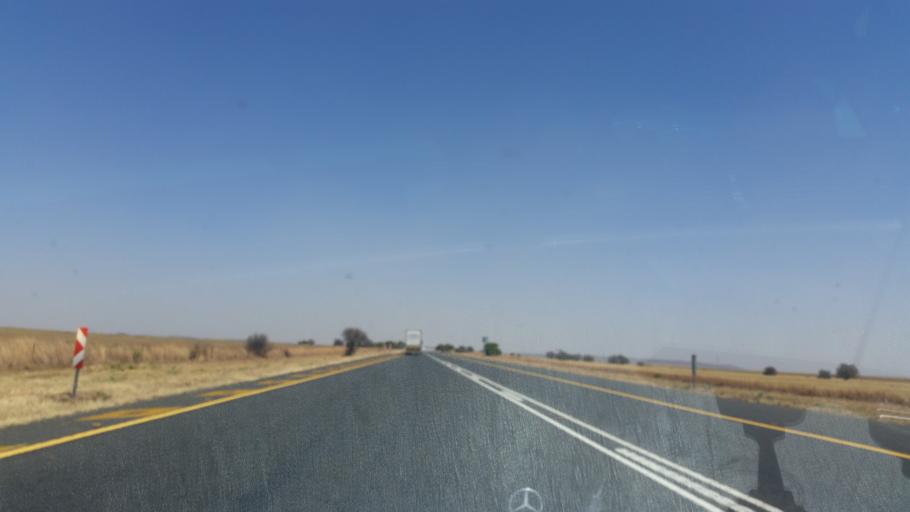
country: ZA
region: Orange Free State
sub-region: Lejweleputswa District Municipality
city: Winburg
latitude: -28.6478
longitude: 26.8796
